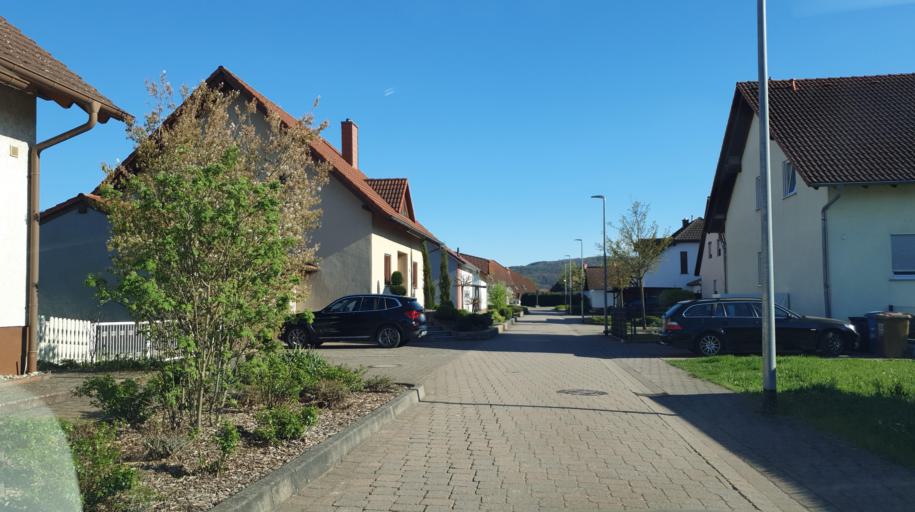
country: DE
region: Rheinland-Pfalz
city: Bruchmuhlbach-Miesau
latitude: 49.4010
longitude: 7.4395
